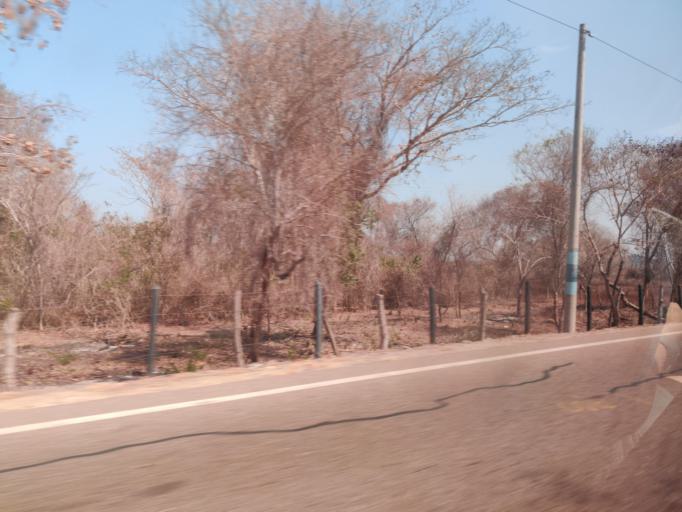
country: CO
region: Bolivar
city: Turbana
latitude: 10.2152
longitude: -75.5944
